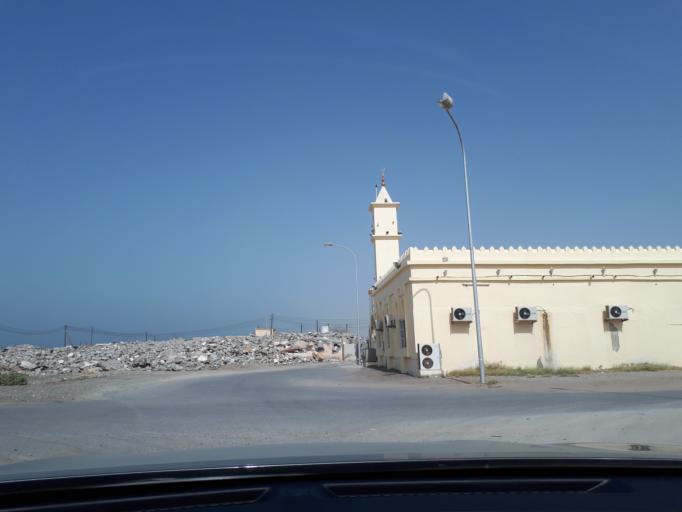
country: OM
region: Al Batinah
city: Barka'
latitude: 23.7086
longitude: 57.9018
